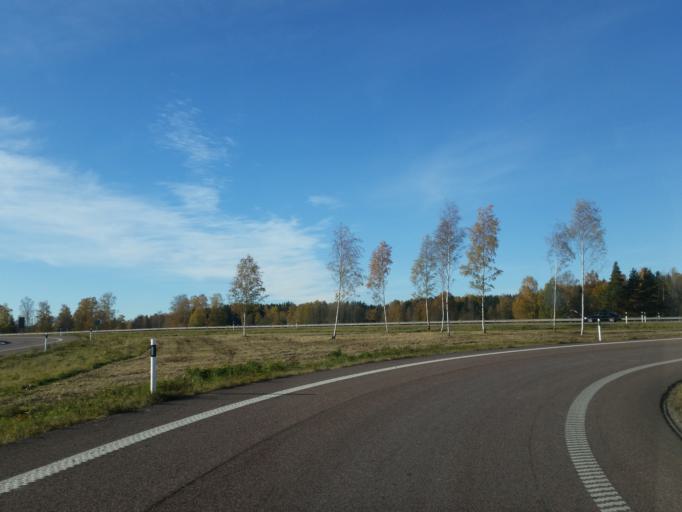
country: SE
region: Dalarna
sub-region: Borlange Kommun
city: Ornas
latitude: 60.5036
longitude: 15.5222
